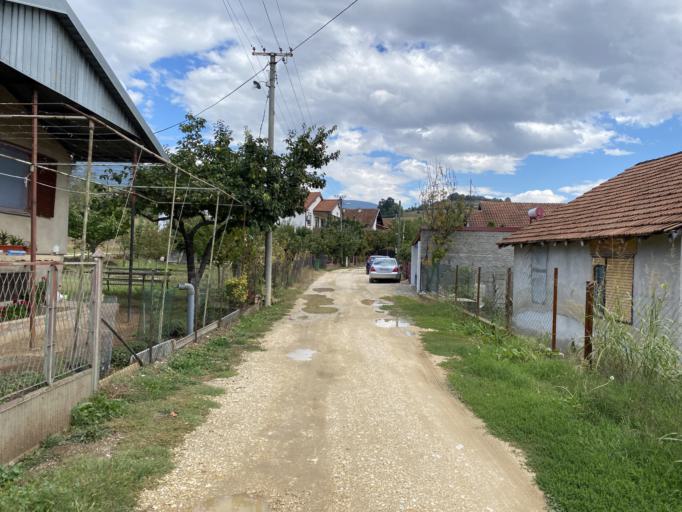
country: MK
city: Radishani
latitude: 42.0816
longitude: 21.4497
